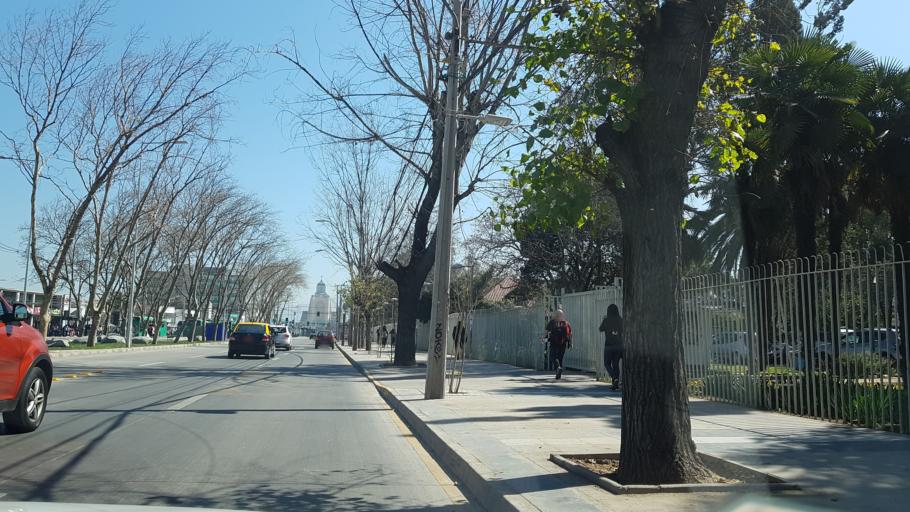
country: CL
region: Santiago Metropolitan
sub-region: Provincia de Santiago
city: Lo Prado
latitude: -33.5104
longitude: -70.7536
